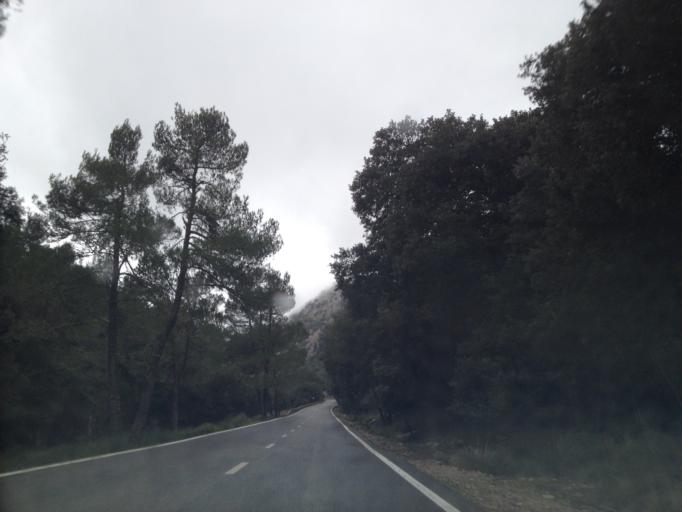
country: ES
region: Balearic Islands
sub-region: Illes Balears
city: Fornalutx
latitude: 39.7907
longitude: 2.7835
